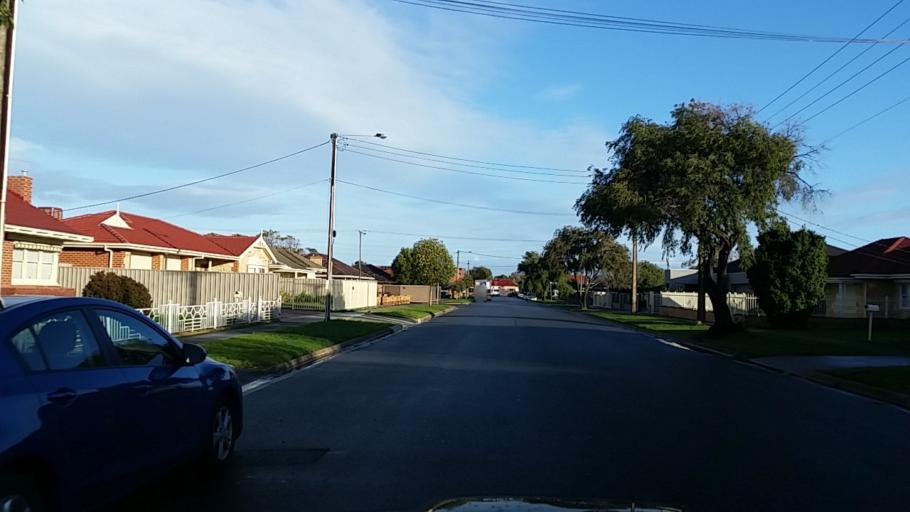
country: AU
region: South Australia
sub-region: Charles Sturt
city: Findon
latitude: -34.9030
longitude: 138.5371
